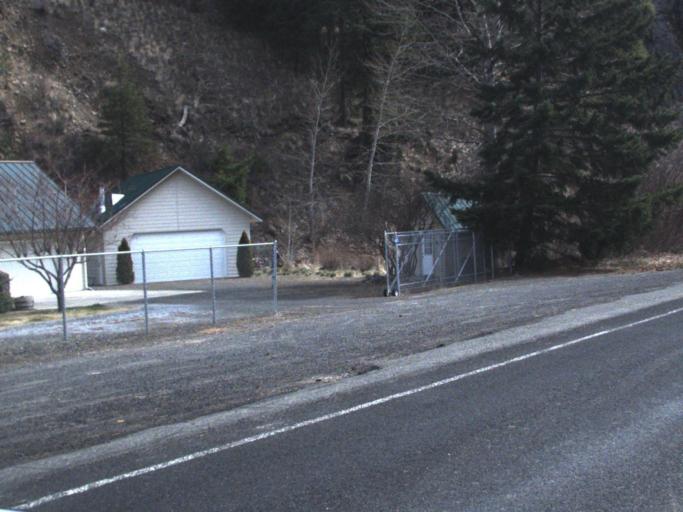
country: US
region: Washington
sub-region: Kittitas County
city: Cle Elum
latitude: 46.8942
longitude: -121.0023
